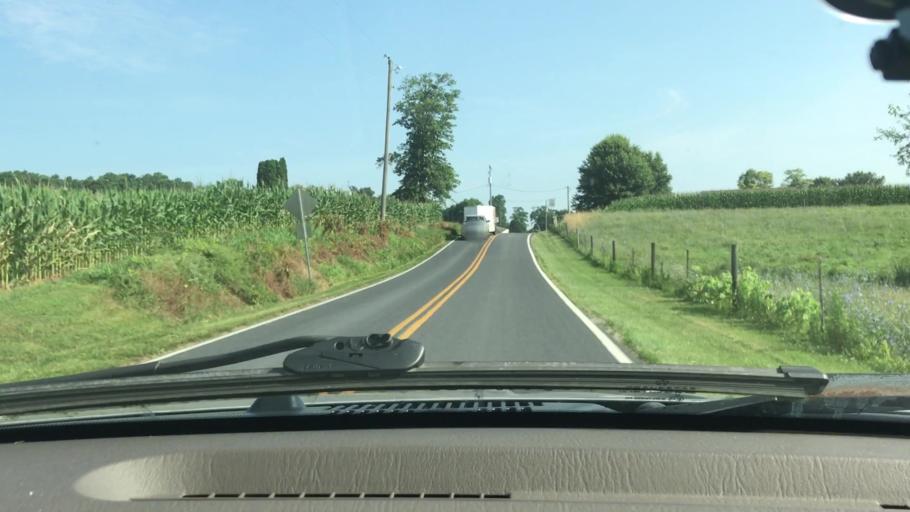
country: US
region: Pennsylvania
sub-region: Lancaster County
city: Rheems
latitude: 40.1493
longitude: -76.5715
